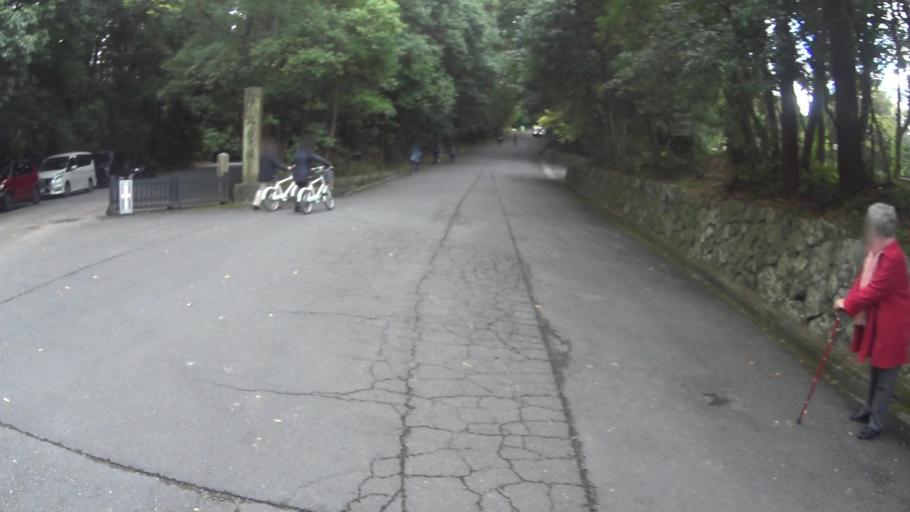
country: JP
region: Kyoto
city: Kyoto
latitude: 34.9795
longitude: 135.7792
